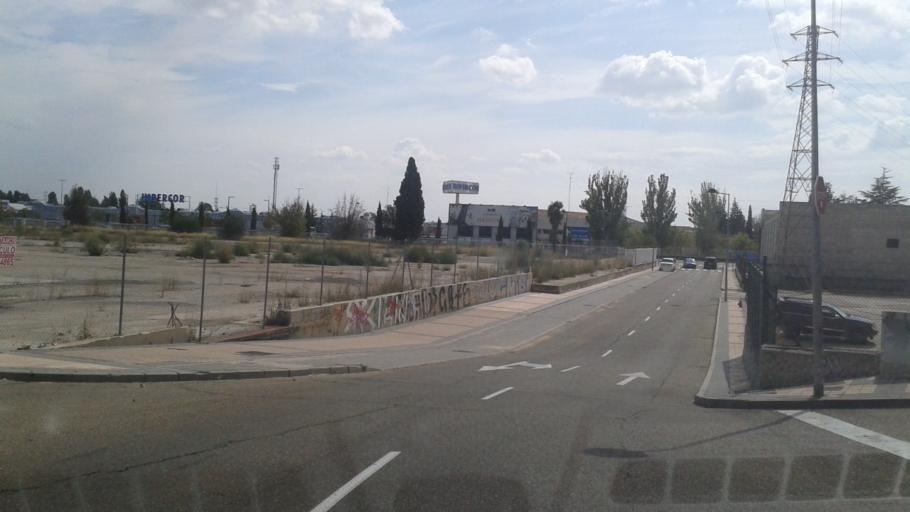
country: ES
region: Castille and Leon
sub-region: Provincia de Valladolid
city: Arroyo
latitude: 41.6244
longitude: -4.7730
